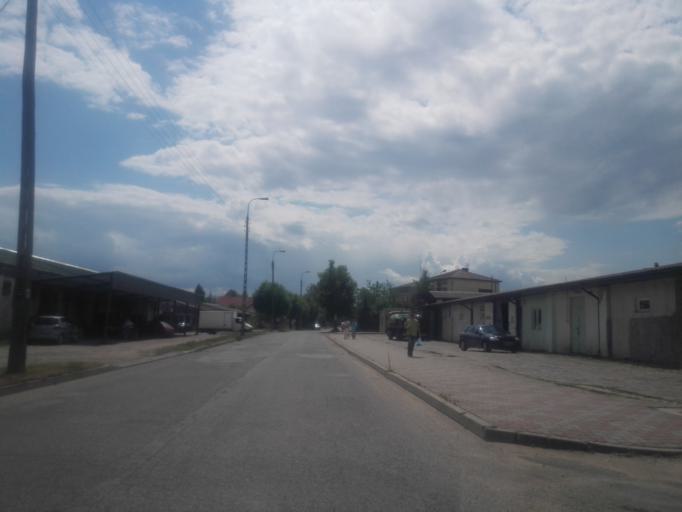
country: PL
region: Podlasie
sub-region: Powiat sejnenski
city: Sejny
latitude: 54.1140
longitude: 23.3527
